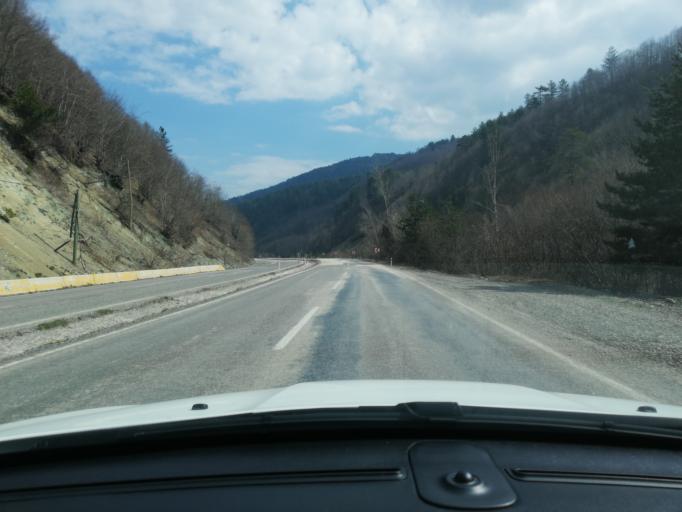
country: TR
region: Kastamonu
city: Kuzyaka
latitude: 41.1314
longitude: 33.7723
